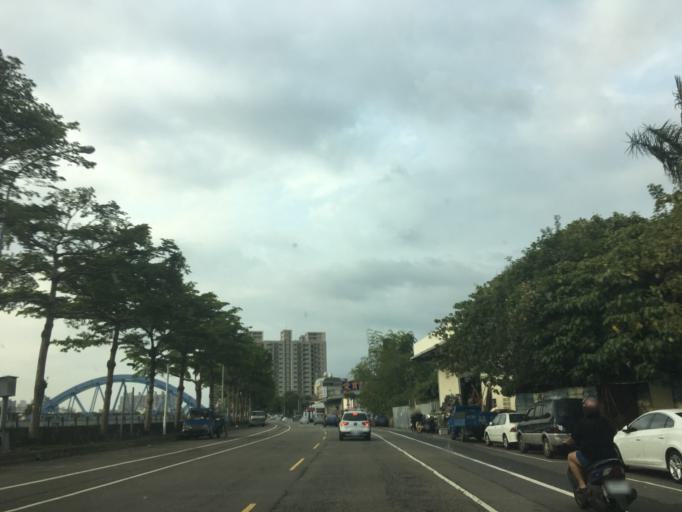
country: TW
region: Taiwan
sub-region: Taichung City
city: Taichung
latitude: 24.1562
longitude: 120.7047
